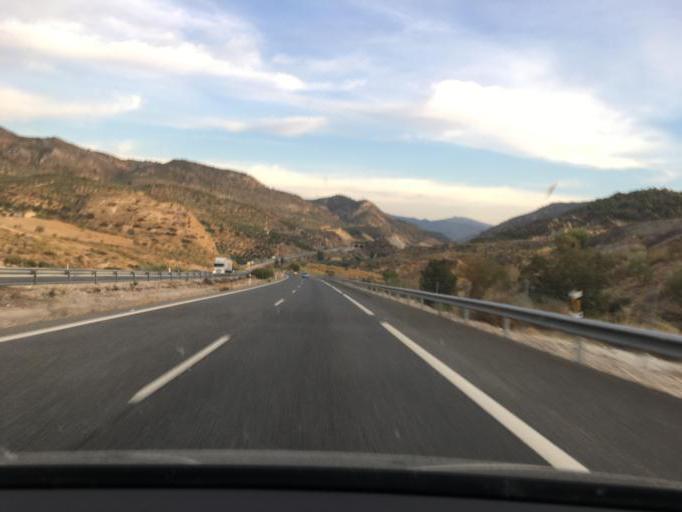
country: ES
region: Andalusia
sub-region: Provincia de Jaen
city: Pegalajar
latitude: 37.7157
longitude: -3.6472
